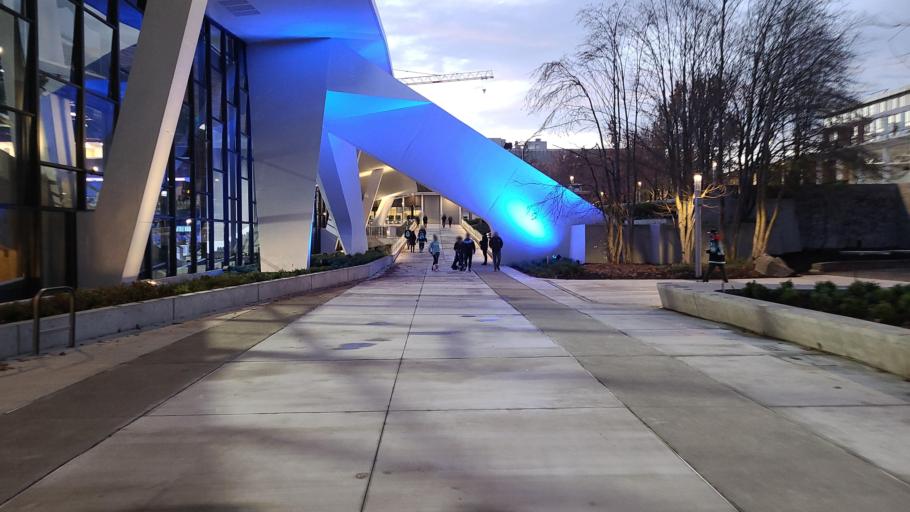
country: US
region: Washington
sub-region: King County
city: Seattle
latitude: 47.6226
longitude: -122.3535
